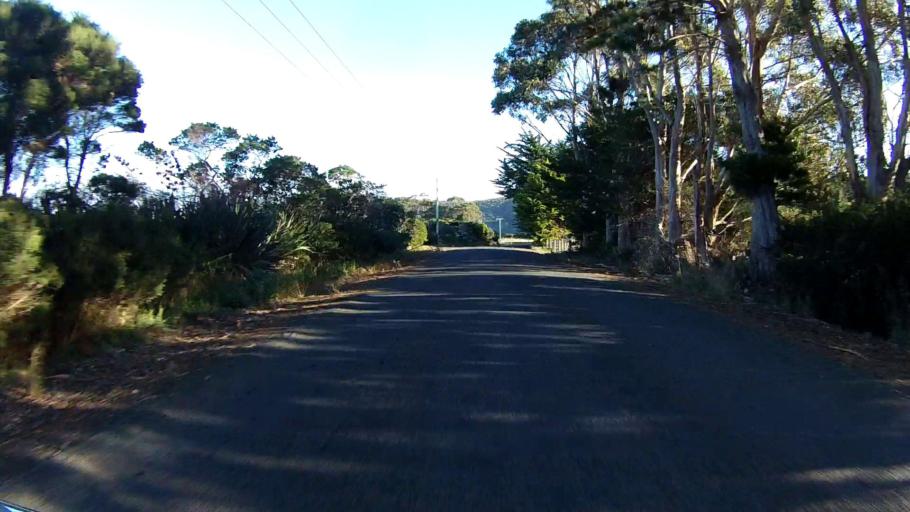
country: AU
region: Tasmania
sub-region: Clarence
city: Sandford
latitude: -43.1698
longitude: 147.8573
